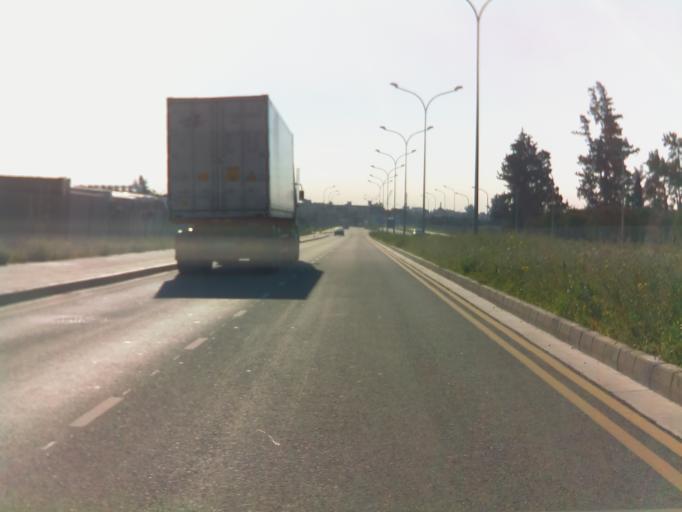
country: CY
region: Limassol
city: Ypsonas
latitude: 34.6627
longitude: 32.9932
